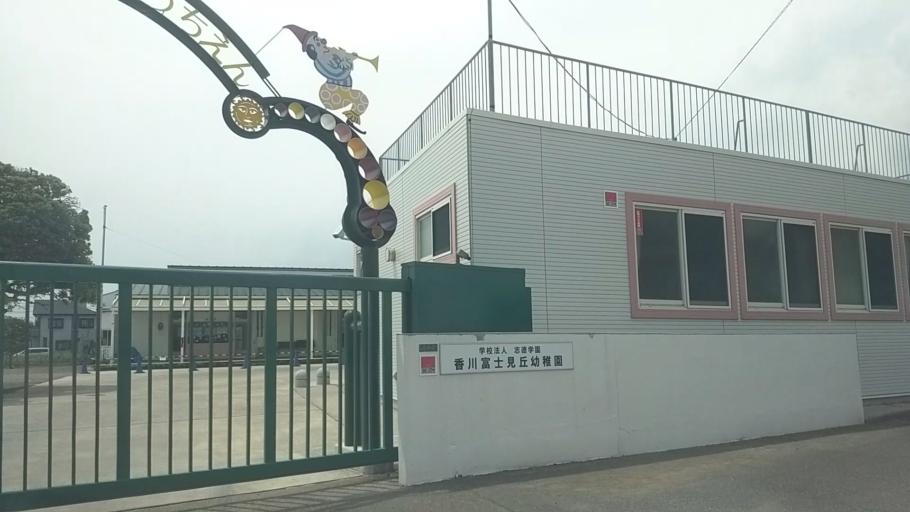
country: JP
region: Kanagawa
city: Chigasaki
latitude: 35.3558
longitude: 139.3972
